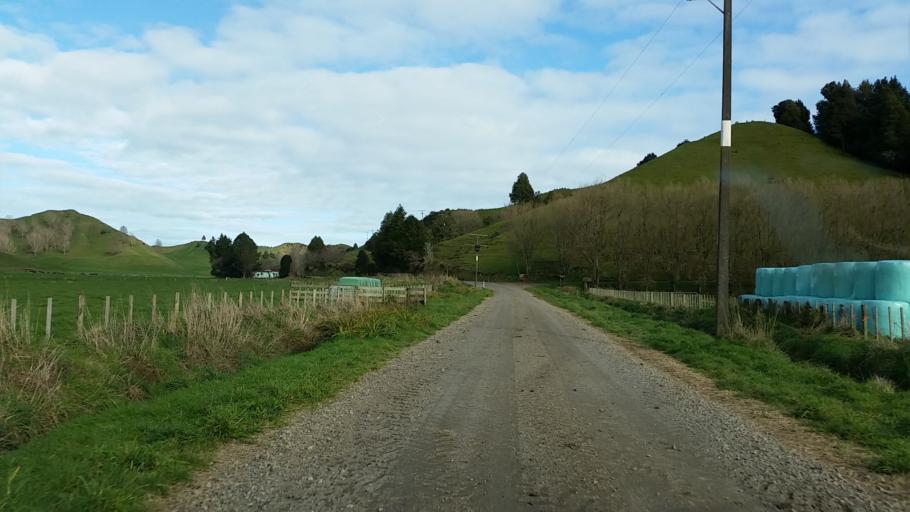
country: NZ
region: Taranaki
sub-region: South Taranaki District
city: Eltham
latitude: -39.2508
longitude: 174.5358
